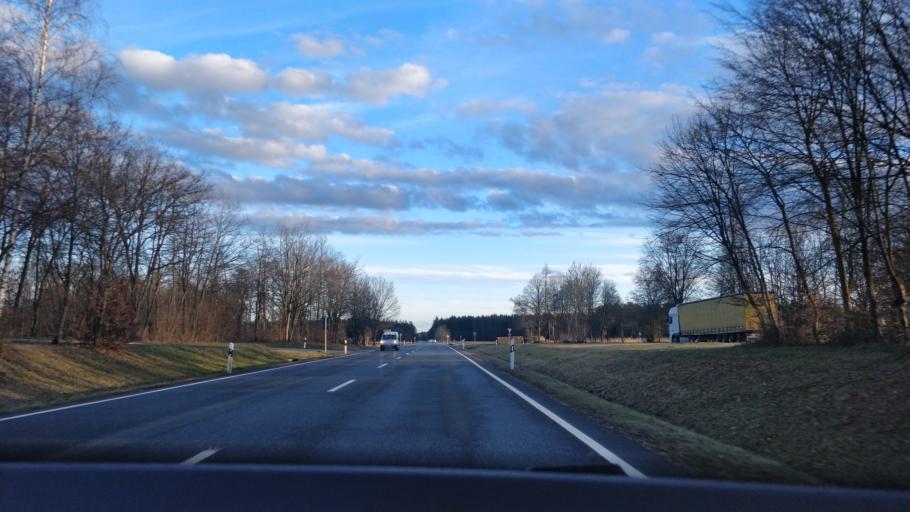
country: DE
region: Bavaria
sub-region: Upper Palatinate
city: Pressath
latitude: 49.7564
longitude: 11.9296
